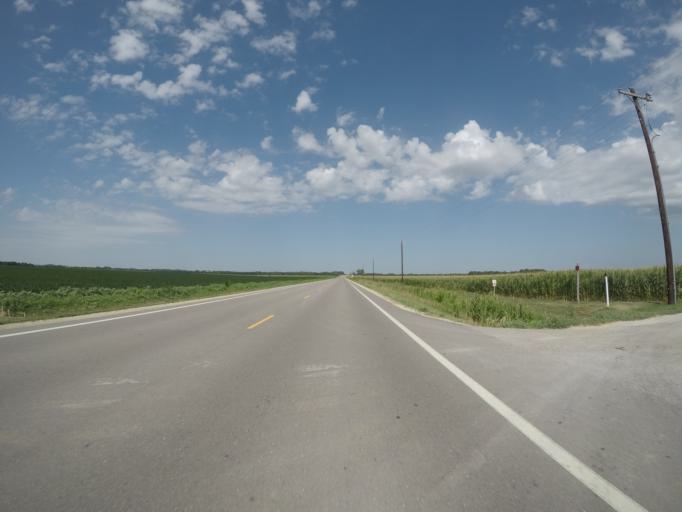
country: US
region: Kansas
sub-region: Clay County
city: Clay Center
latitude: 39.3797
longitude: -97.2147
